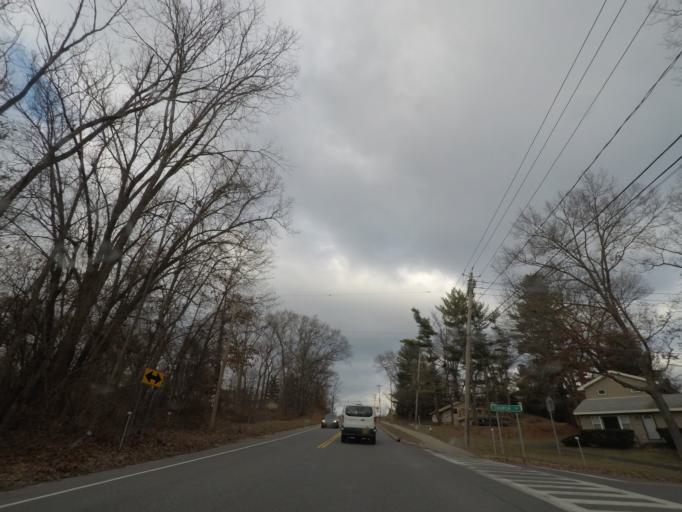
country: US
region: New York
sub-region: Albany County
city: Westmere
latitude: 42.6810
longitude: -73.8724
